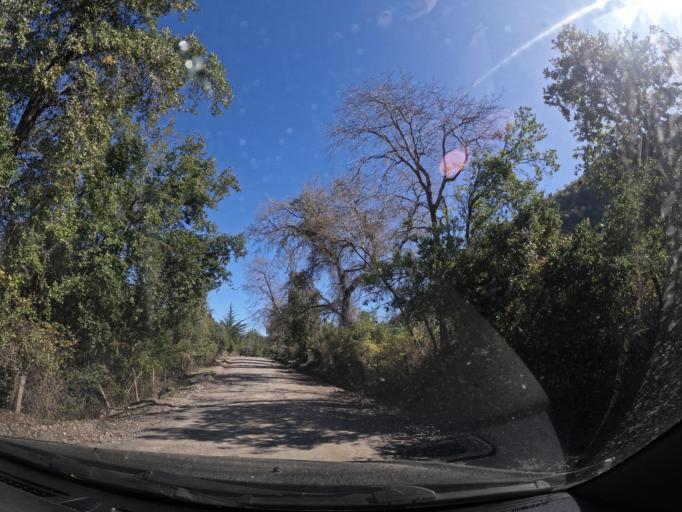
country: CL
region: Maule
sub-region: Provincia de Linares
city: Longavi
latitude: -36.2284
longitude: -71.3966
